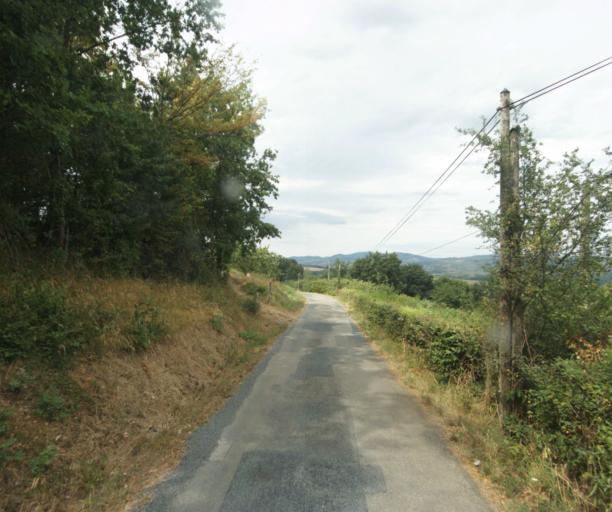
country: FR
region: Rhone-Alpes
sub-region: Departement du Rhone
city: Bully
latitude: 45.8798
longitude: 4.5710
